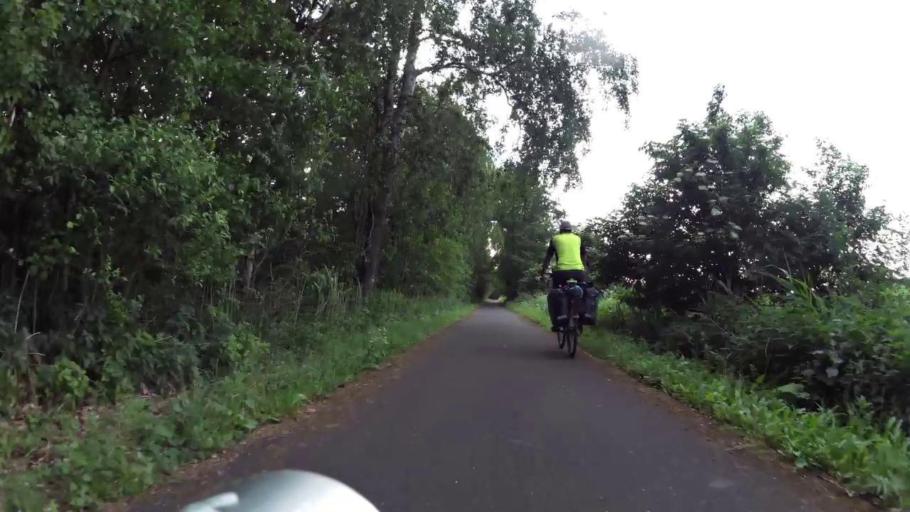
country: PL
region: Kujawsko-Pomorskie
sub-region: Powiat chelminski
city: Unislaw
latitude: 53.1861
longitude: 18.3795
